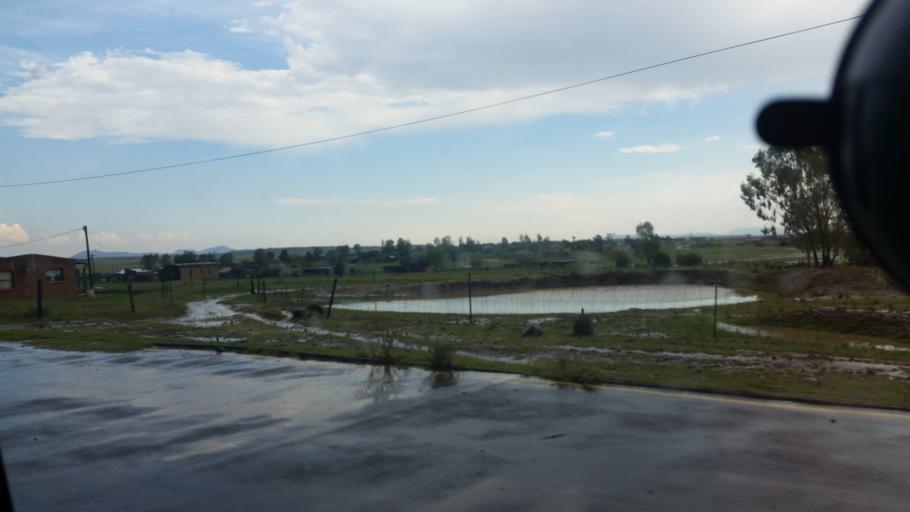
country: LS
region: Mafeteng
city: Mafeteng
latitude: -29.7666
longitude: 27.1794
